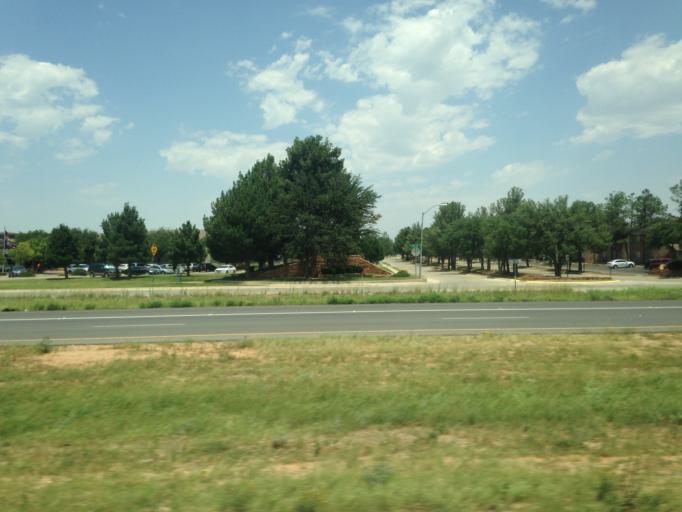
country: US
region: Texas
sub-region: Midland County
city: Midland
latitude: 32.0389
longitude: -102.1081
